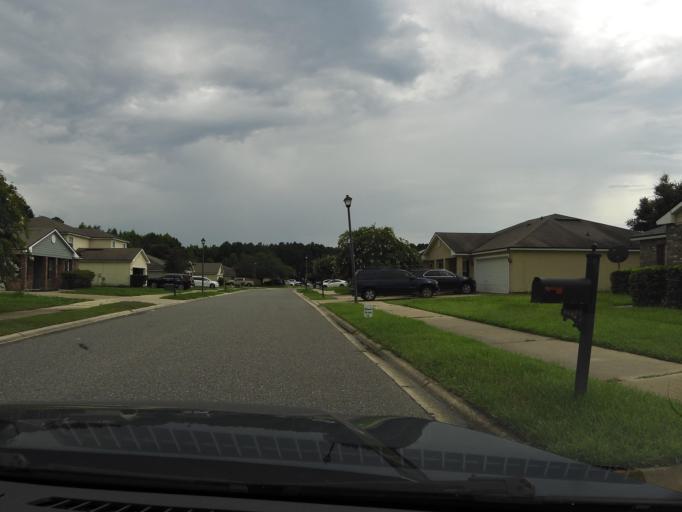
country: US
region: Florida
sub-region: Nassau County
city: Nassau Village-Ratliff
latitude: 30.4403
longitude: -81.7528
